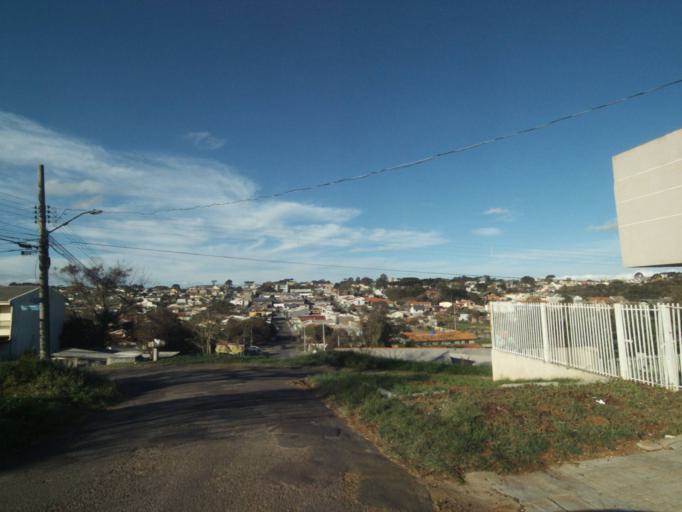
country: BR
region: Parana
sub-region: Curitiba
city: Curitiba
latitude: -25.3828
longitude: -49.2493
